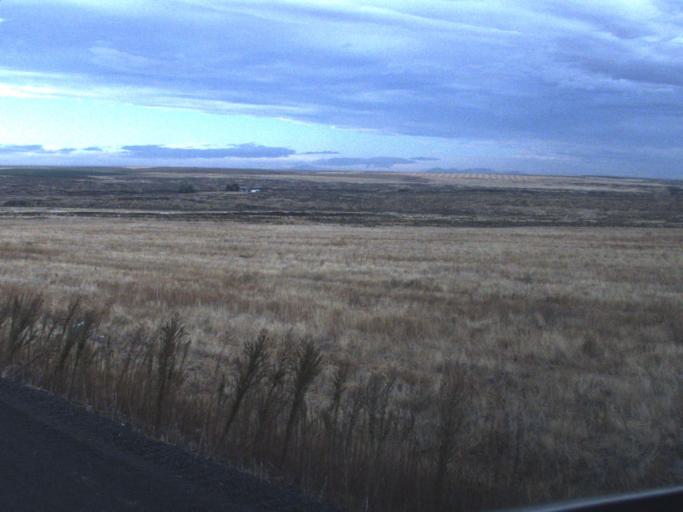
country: US
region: Washington
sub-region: Adams County
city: Ritzville
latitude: 47.4532
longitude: -118.7471
